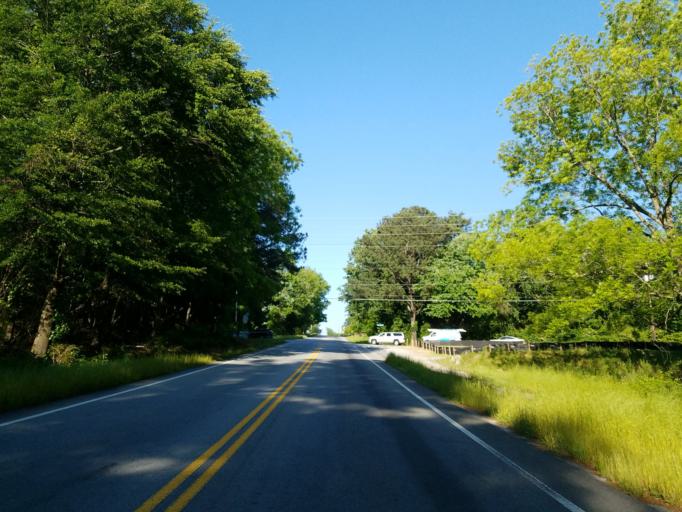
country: US
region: Georgia
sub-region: Douglas County
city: Douglasville
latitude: 33.7263
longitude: -84.8284
